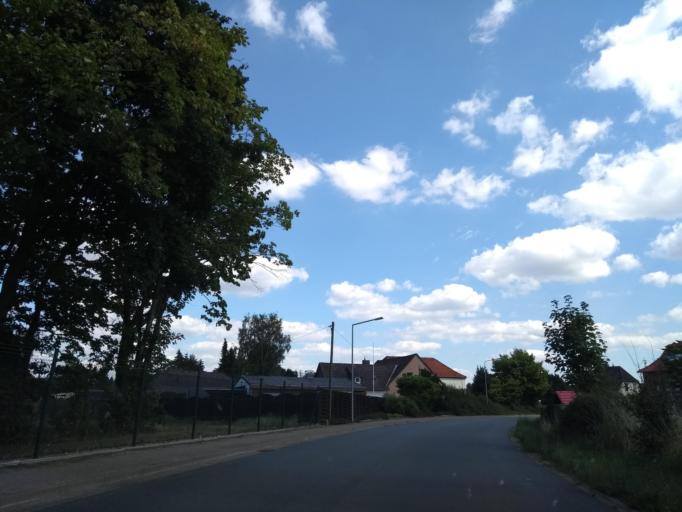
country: DE
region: Lower Saxony
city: Wunstorf
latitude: 52.4527
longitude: 9.4166
